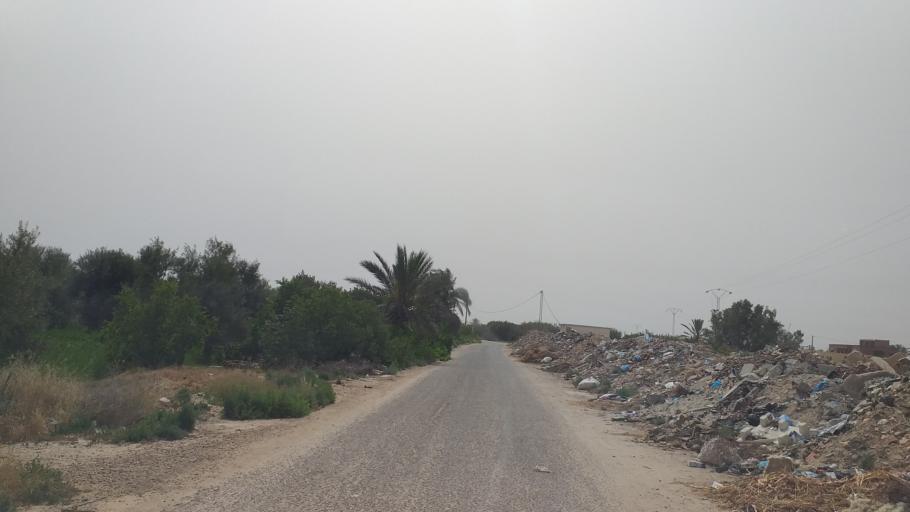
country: TN
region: Qabis
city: Gabes
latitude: 33.9462
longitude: 10.0498
